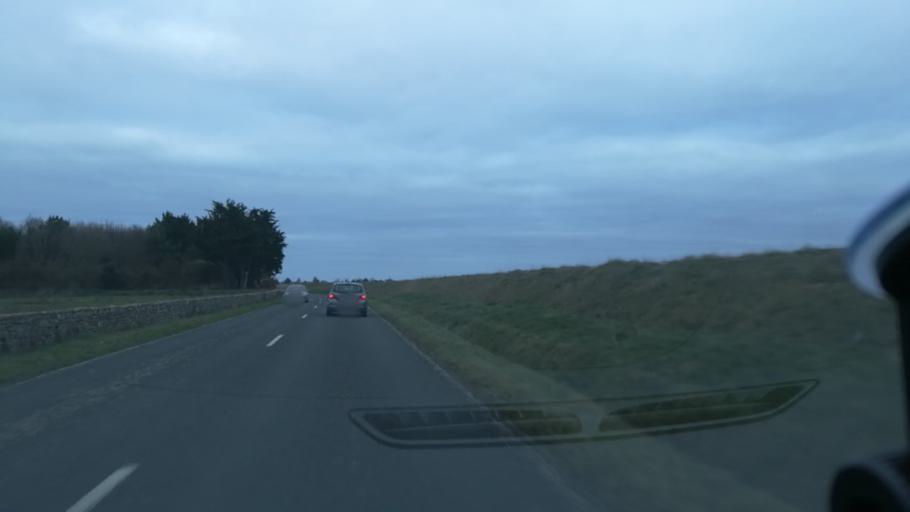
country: FR
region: Lower Normandy
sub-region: Departement de la Manche
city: Saint-Vaast-la-Hougue
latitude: 49.6001
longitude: -1.2621
